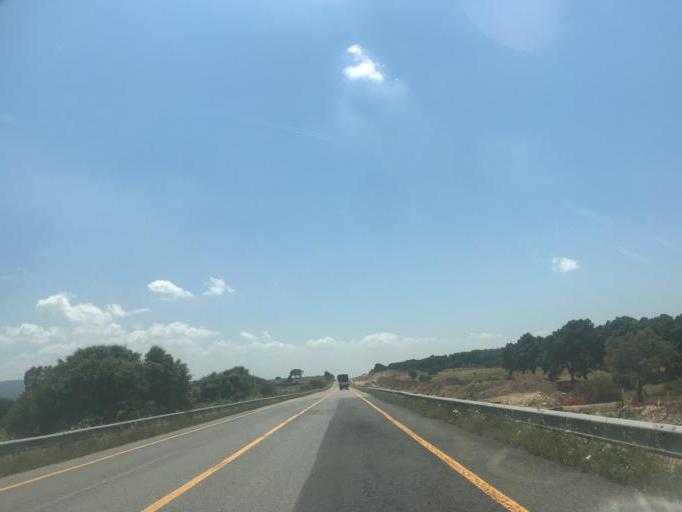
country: IT
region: Sardinia
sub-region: Provincia di Olbia-Tempio
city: Monti
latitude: 40.7907
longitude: 9.2620
